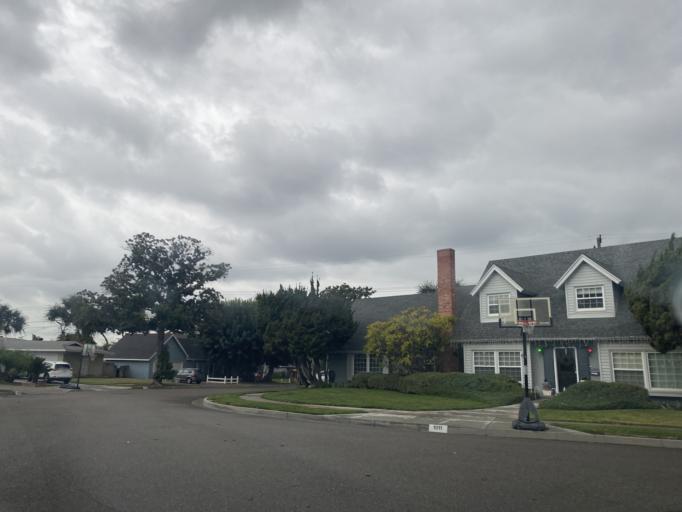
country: US
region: California
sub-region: Orange County
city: Fullerton
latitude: 33.8769
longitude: -117.9092
